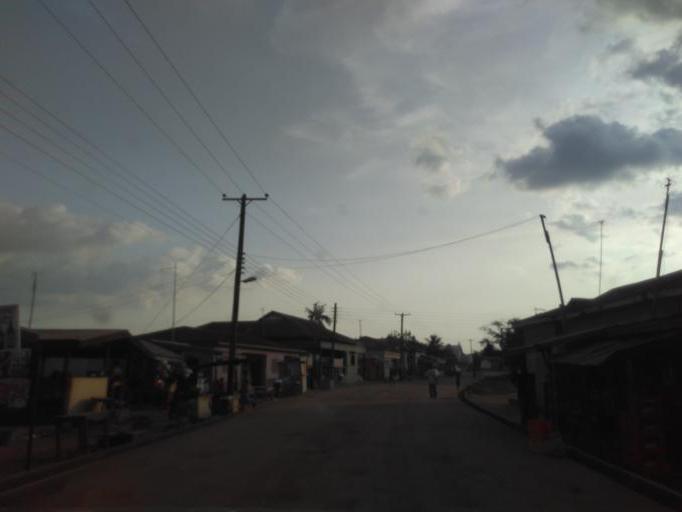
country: GH
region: Ashanti
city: Mamponteng
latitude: 6.6851
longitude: -1.4402
